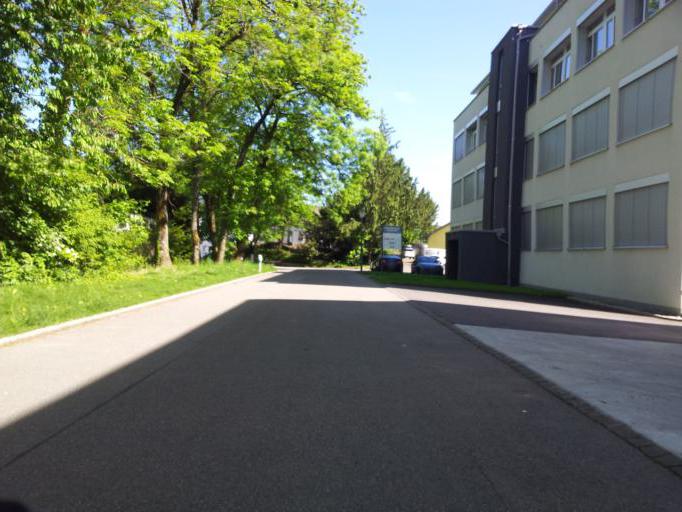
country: CH
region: Zurich
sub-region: Bezirk Dietikon
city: Dietikon / Hofacker
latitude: 47.3951
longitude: 8.4148
